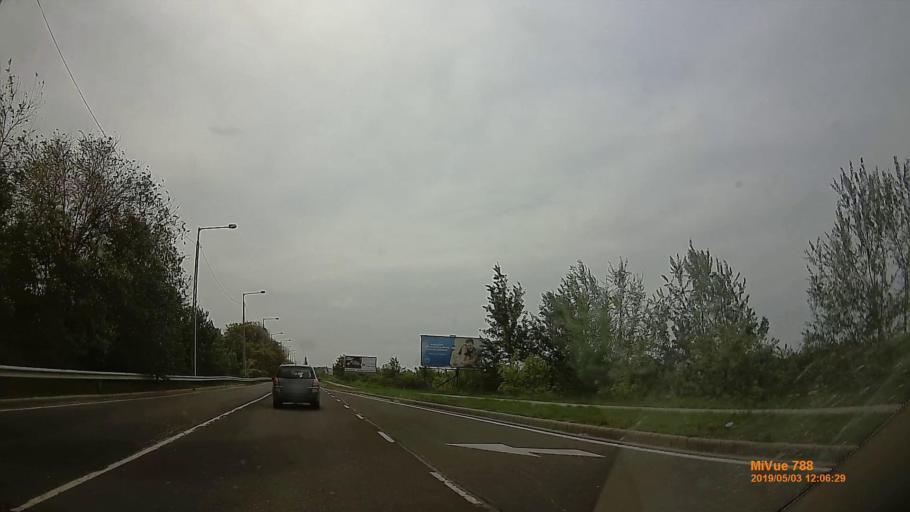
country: HU
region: Jasz-Nagykun-Szolnok
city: Szolnok
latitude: 47.1611
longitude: 20.2032
